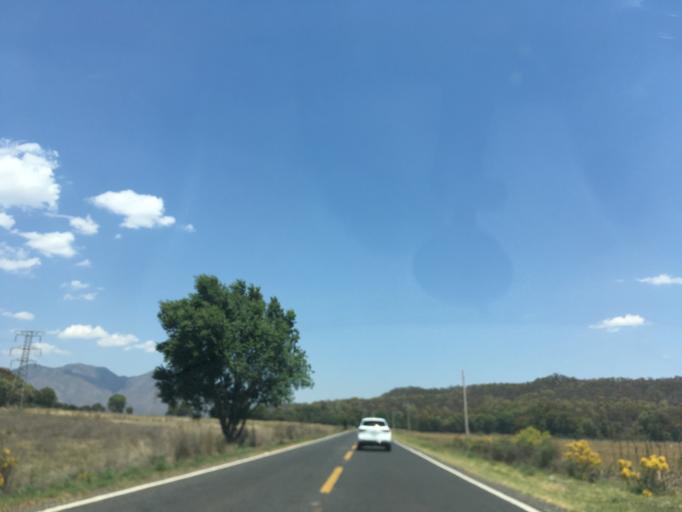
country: MX
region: Michoacan
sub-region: Chilchota
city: Tacuro (Santa Maria Tacuro)
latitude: 19.8170
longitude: -102.0281
